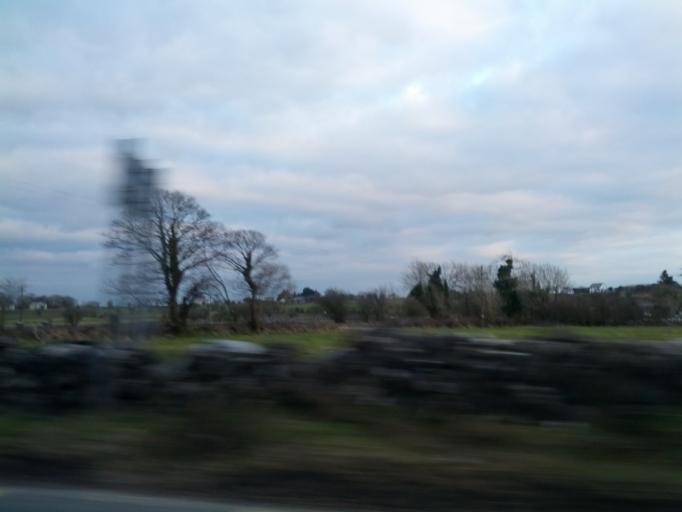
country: IE
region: Connaught
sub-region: County Galway
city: Claregalway
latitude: 53.3845
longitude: -8.8506
